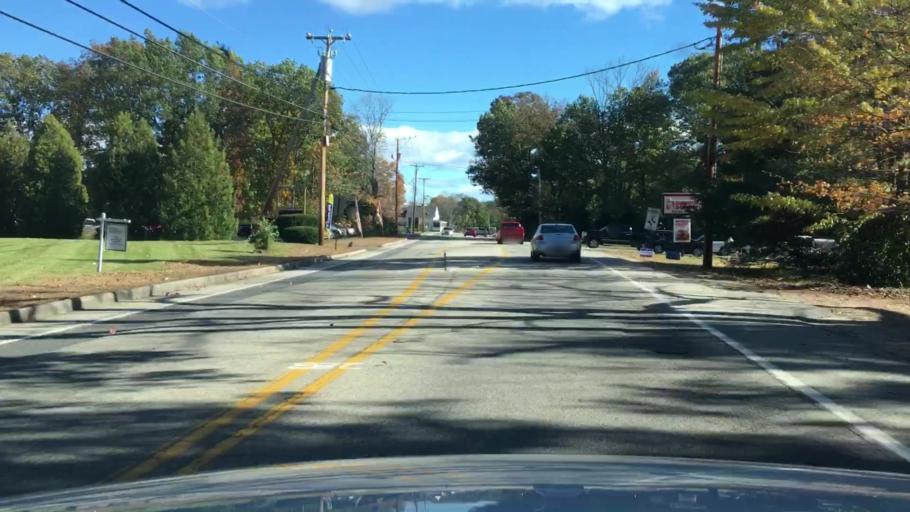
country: US
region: Maine
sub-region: York County
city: South Sanford
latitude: 43.4085
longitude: -70.7378
